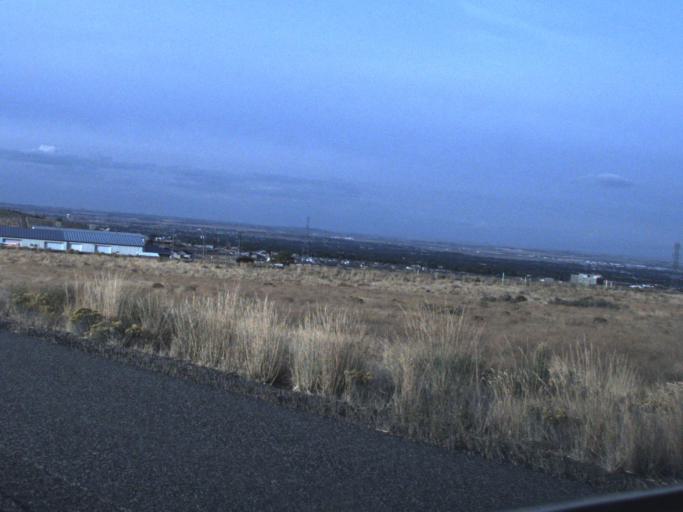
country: US
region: Washington
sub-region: Benton County
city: Kennewick
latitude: 46.1663
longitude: -119.2027
